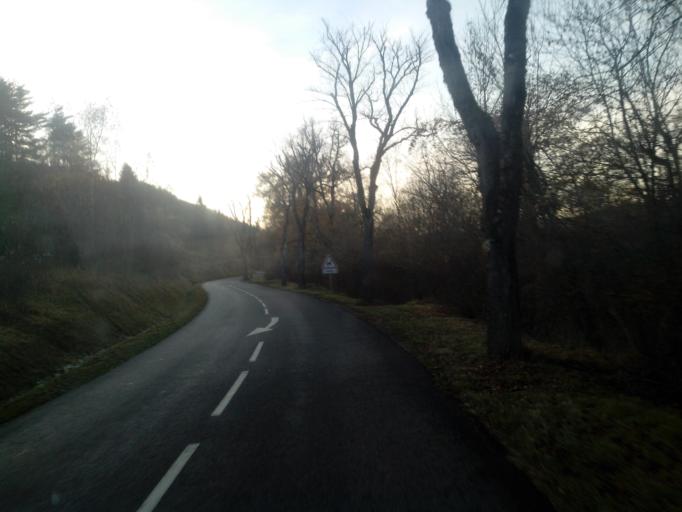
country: FR
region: Languedoc-Roussillon
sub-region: Departement de l'Aude
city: Chalabre
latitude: 42.9099
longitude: 2.0064
